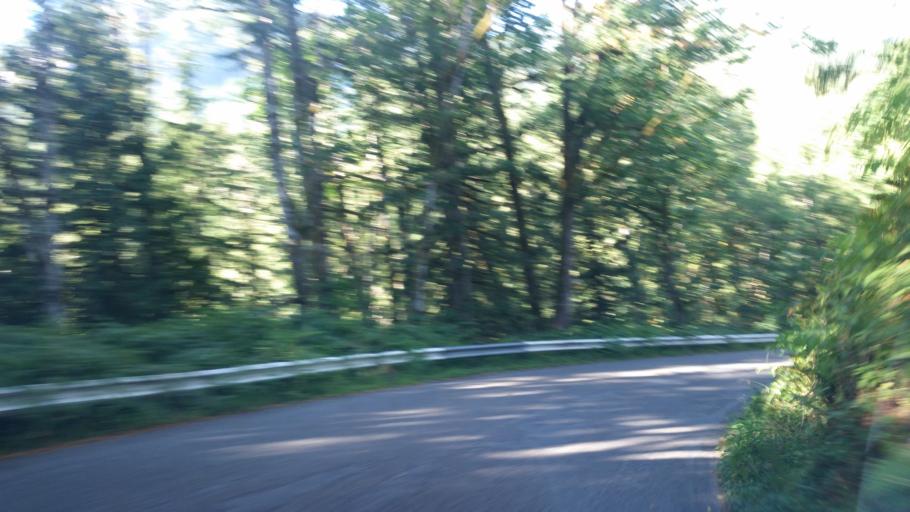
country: US
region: Washington
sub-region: Snohomish County
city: Gold Bar
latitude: 47.8369
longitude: -121.6060
